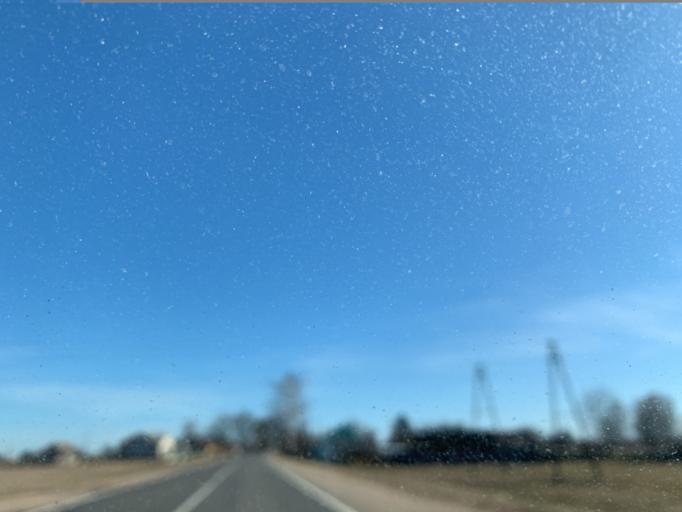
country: BY
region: Minsk
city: Nyasvizh
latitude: 53.2269
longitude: 26.7147
